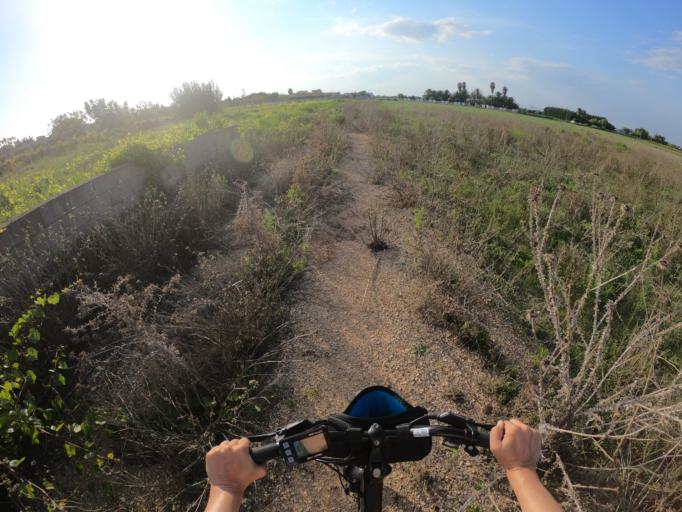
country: IT
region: Apulia
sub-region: Provincia di Lecce
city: Nardo
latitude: 40.1646
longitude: 18.0162
